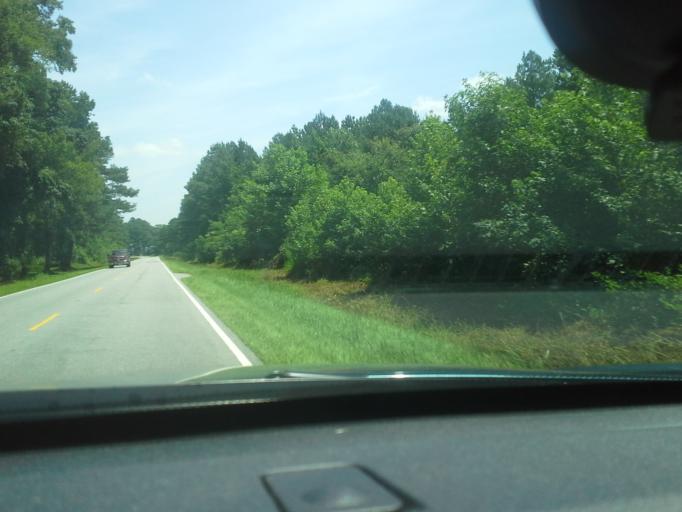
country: US
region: North Carolina
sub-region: Washington County
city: Plymouth
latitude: 35.9103
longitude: -76.6573
